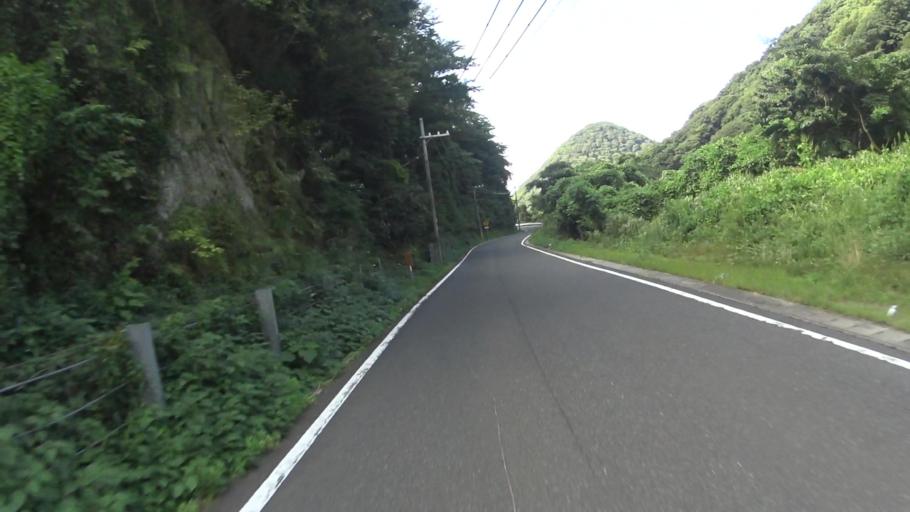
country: JP
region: Kyoto
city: Miyazu
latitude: 35.7678
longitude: 135.2277
